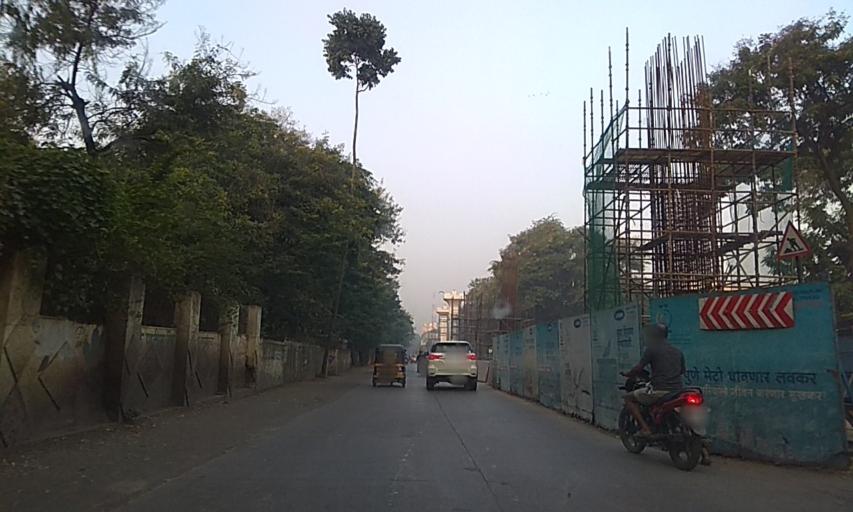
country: IN
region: Maharashtra
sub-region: Pune Division
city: Shivaji Nagar
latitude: 18.5301
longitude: 73.8676
